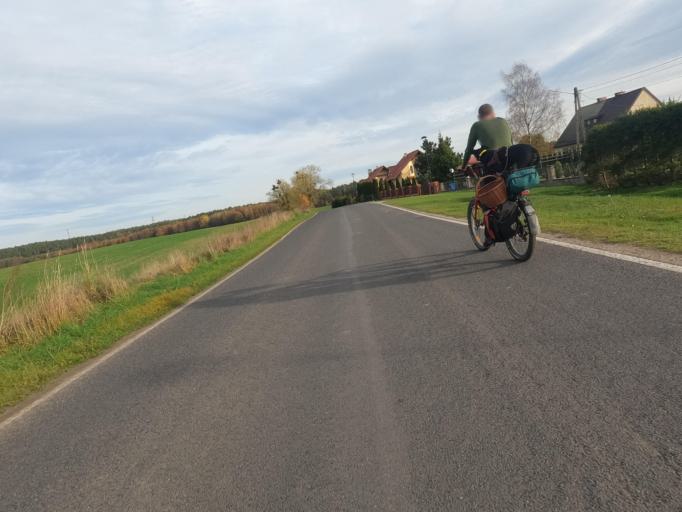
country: PL
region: Pomeranian Voivodeship
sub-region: Powiat starogardzki
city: Skarszewy
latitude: 54.0279
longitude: 18.4680
